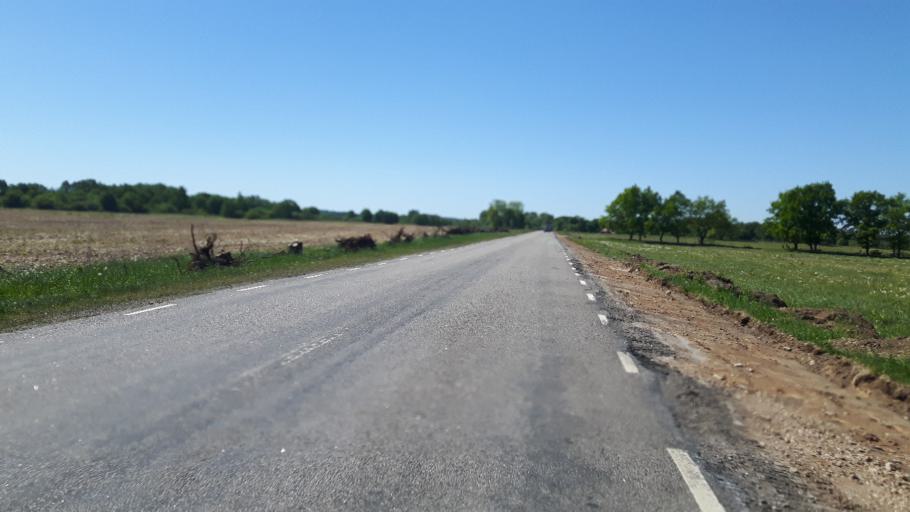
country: EE
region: Ida-Virumaa
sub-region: Narva-Joesuu linn
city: Narva-Joesuu
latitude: 59.3978
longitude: 27.9306
